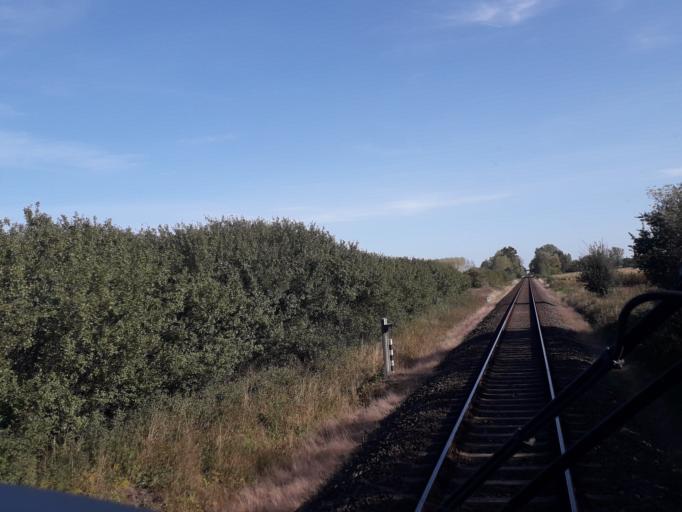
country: DE
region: Brandenburg
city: Velten
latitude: 52.7161
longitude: 13.1255
